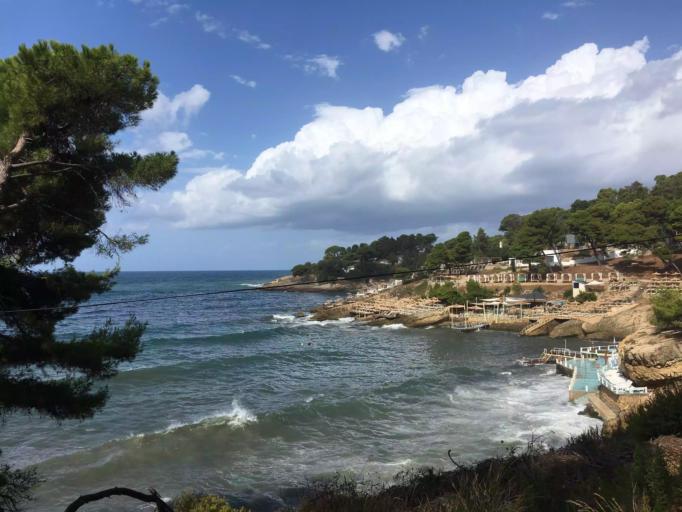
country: ME
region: Ulcinj
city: Ulcinj
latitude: 41.9202
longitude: 19.2115
